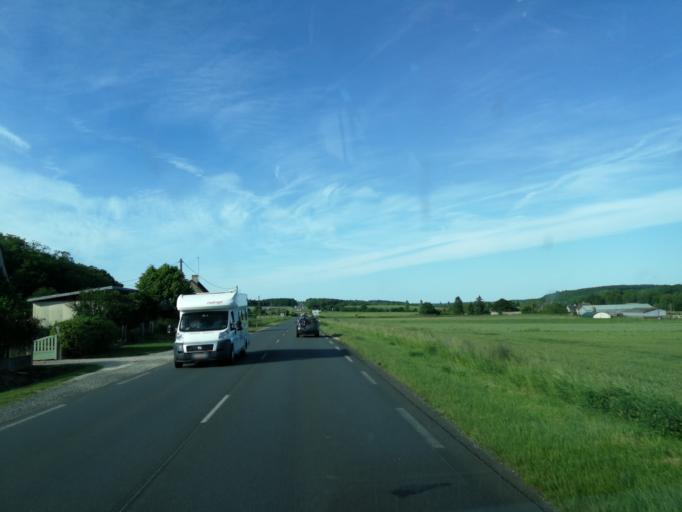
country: FR
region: Centre
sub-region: Departement du Loir-et-Cher
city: Moree
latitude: 47.9351
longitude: 1.2012
